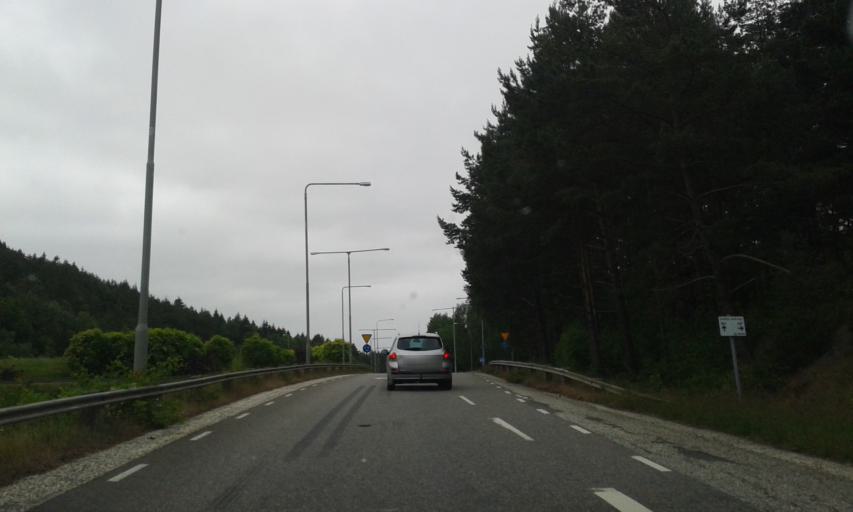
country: SE
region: Vaestra Goetaland
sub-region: Goteborg
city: Eriksbo
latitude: 57.7569
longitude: 12.0453
